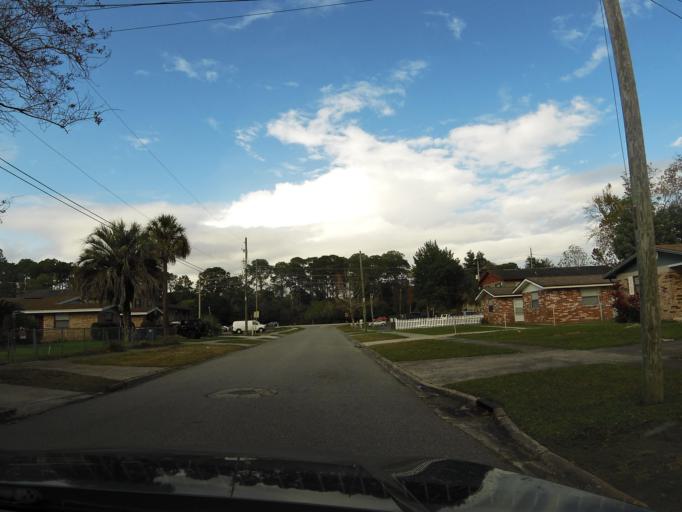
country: US
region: Florida
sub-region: Duval County
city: Jacksonville
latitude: 30.3510
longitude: -81.5653
